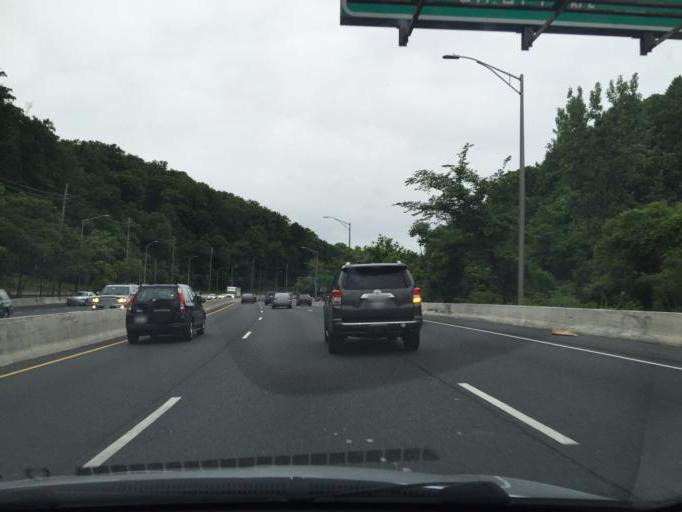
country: US
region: Maryland
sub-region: Baltimore County
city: Towson
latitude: 39.3545
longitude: -76.6481
